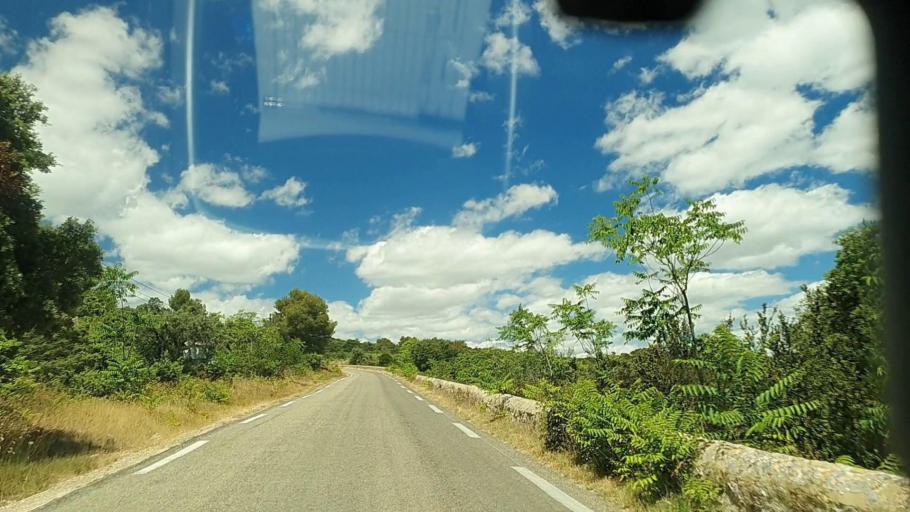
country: FR
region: Languedoc-Roussillon
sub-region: Departement du Gard
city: Cabrieres
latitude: 43.9074
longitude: 4.4736
